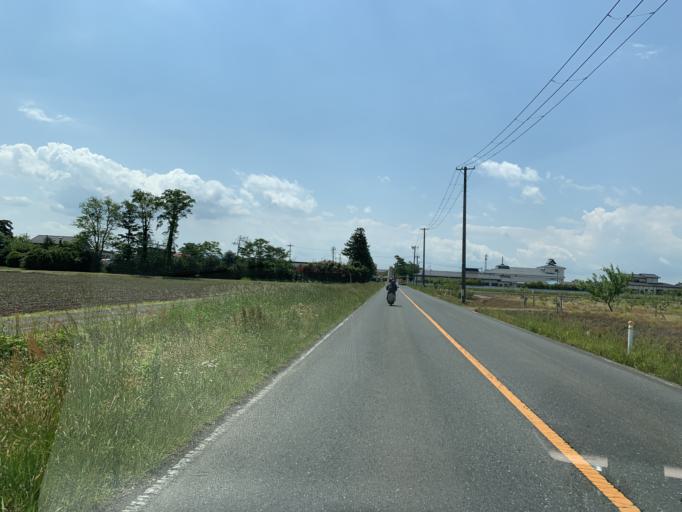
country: JP
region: Miyagi
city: Kogota
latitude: 38.5877
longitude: 141.0314
